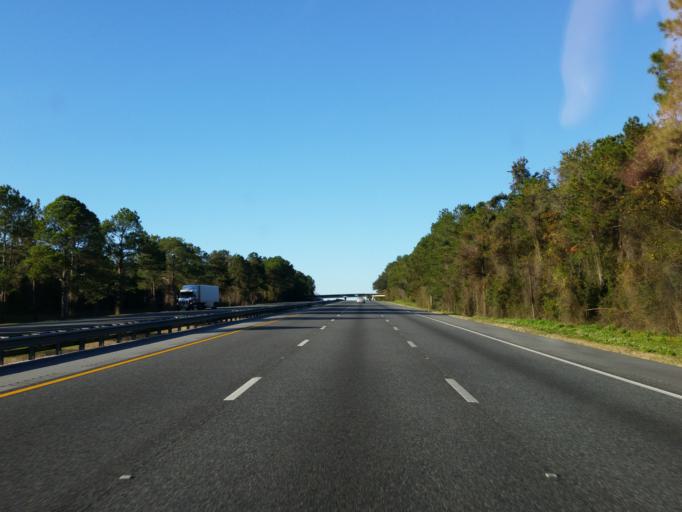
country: US
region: Florida
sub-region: Columbia County
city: Lake City
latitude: 30.0223
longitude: -82.6103
